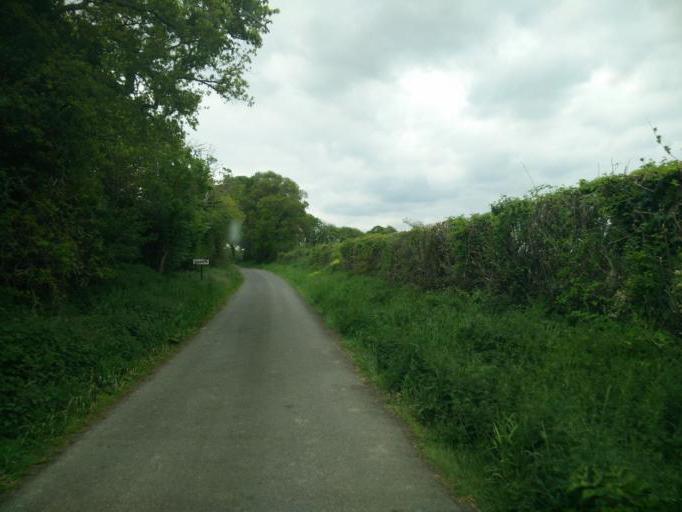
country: FR
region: Brittany
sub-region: Departement des Cotes-d'Armor
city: Hillion
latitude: 48.5121
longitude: -2.6702
